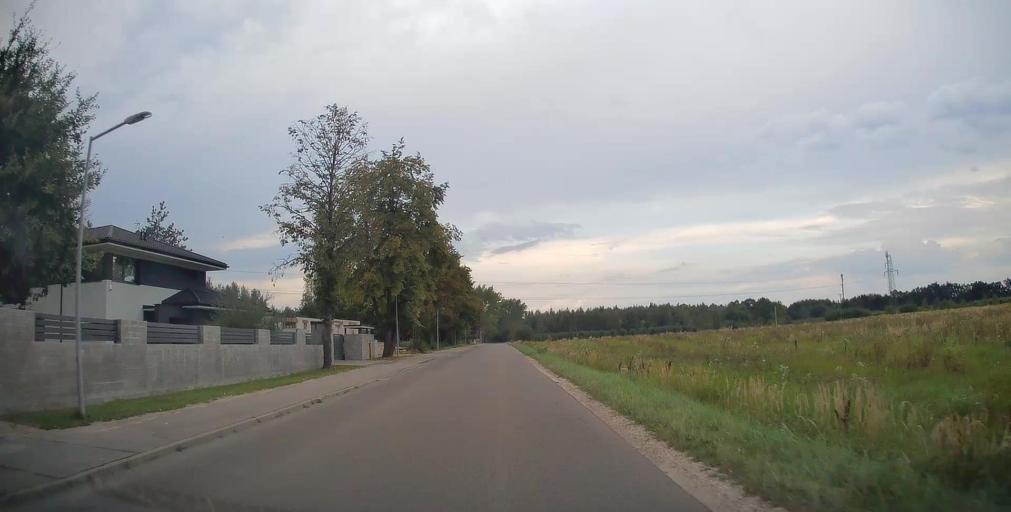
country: PL
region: Masovian Voivodeship
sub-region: Powiat bialobrzeski
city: Sucha
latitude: 51.6294
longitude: 20.9540
